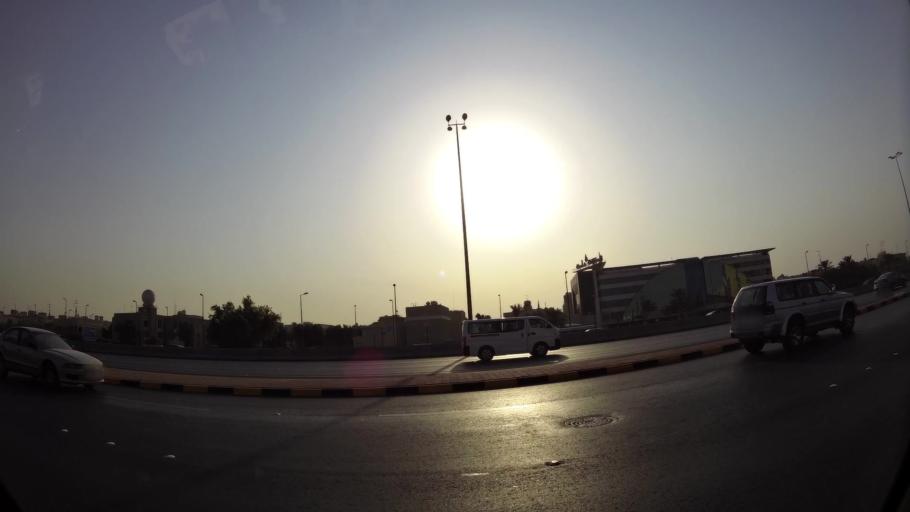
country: KW
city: Bayan
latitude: 29.3219
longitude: 48.0473
